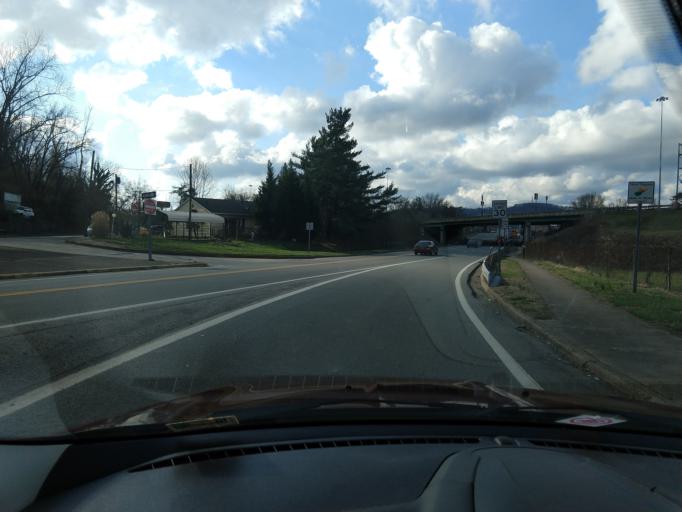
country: US
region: West Virginia
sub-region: Kanawha County
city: Dunbar
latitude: 38.3635
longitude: -81.7370
